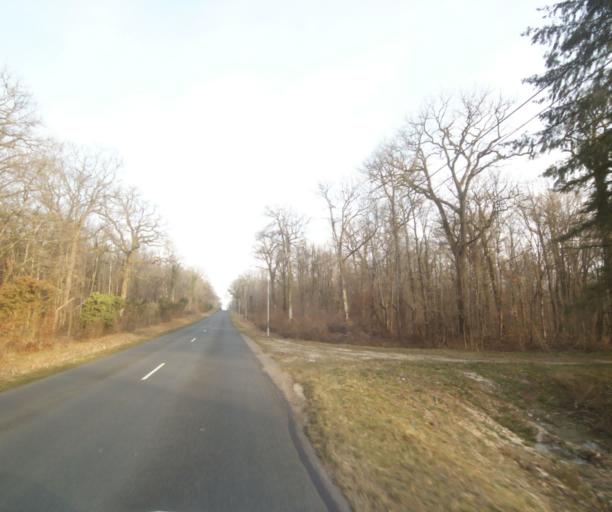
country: FR
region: Champagne-Ardenne
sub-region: Departement de la Haute-Marne
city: Chancenay
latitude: 48.6963
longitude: 4.9454
